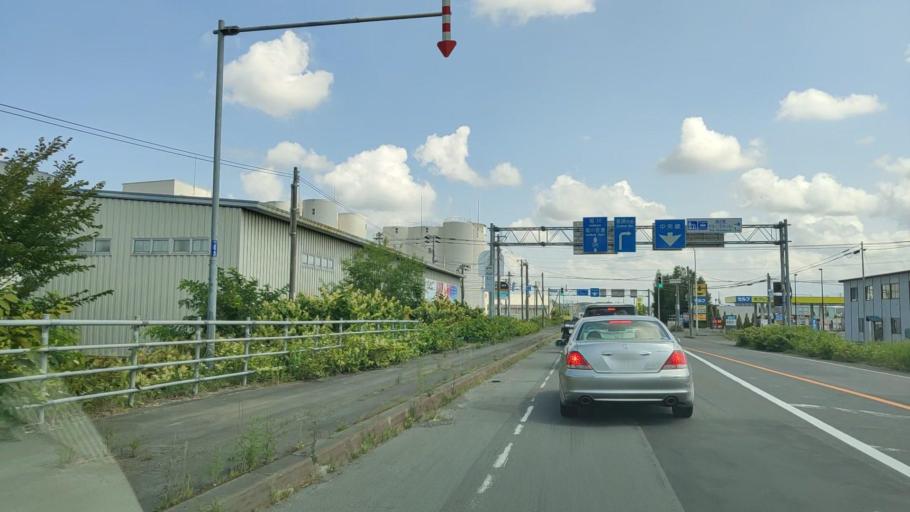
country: JP
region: Hokkaido
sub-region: Asahikawa-shi
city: Asahikawa
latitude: 43.5899
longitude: 142.4525
